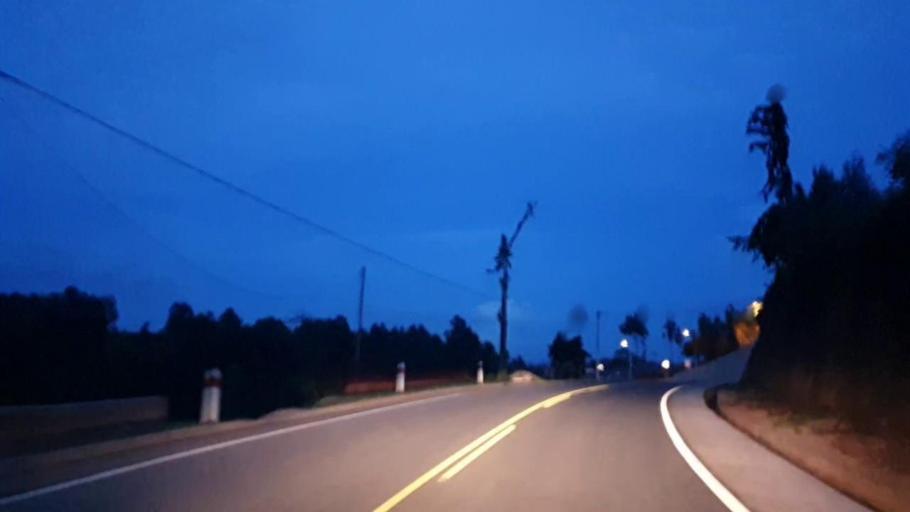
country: RW
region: Southern Province
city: Gikongoro
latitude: -2.4654
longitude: 29.5733
